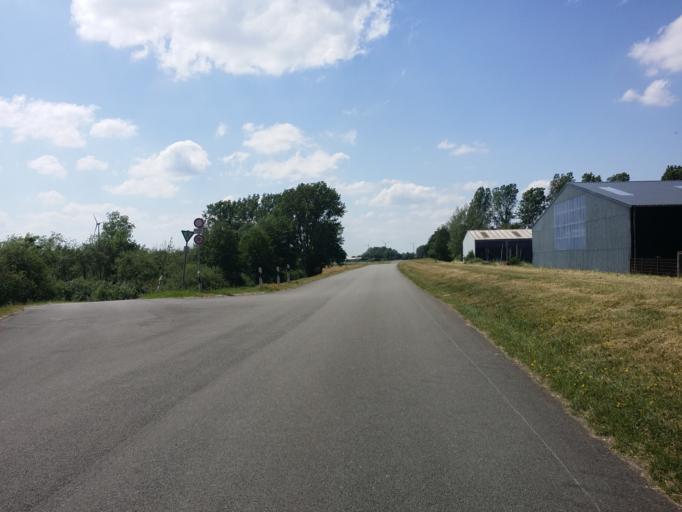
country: DE
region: Lower Saxony
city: Lemwerder
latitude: 53.1214
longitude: 8.6623
